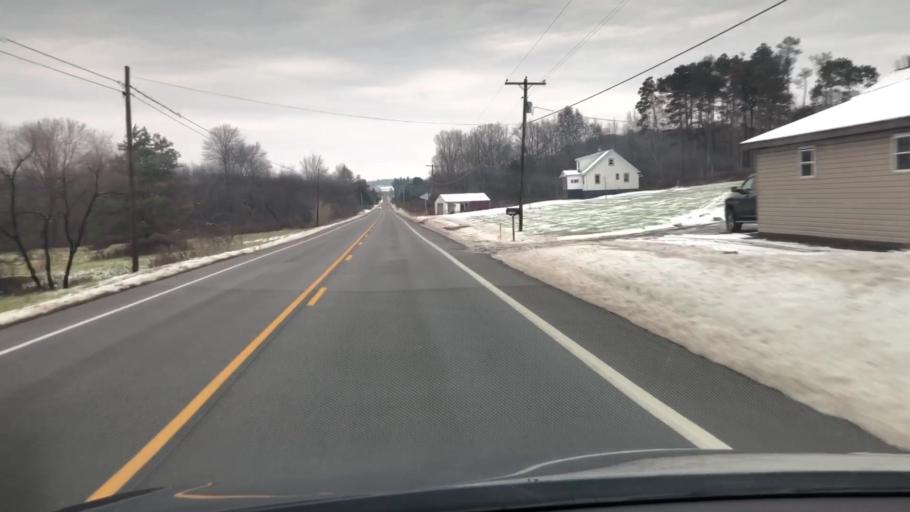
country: US
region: Pennsylvania
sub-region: Jefferson County
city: Brookville
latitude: 41.0874
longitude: -79.2290
